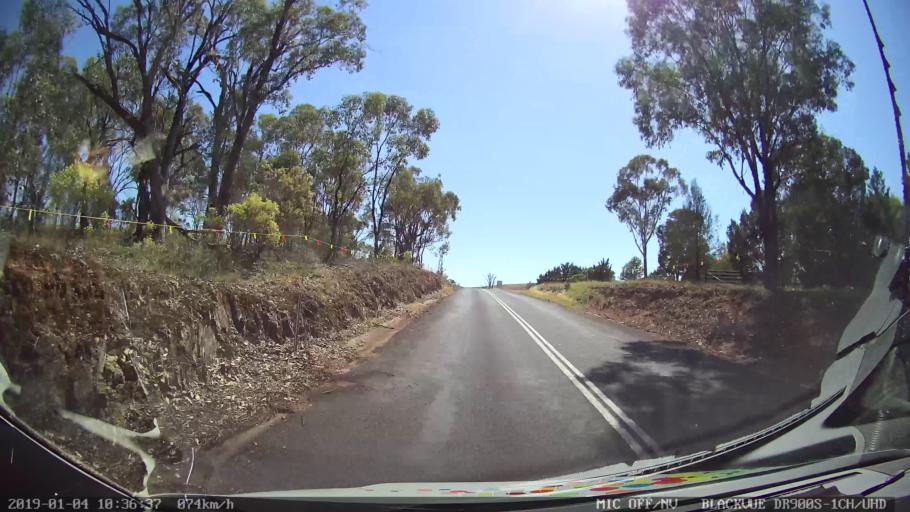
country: AU
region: New South Wales
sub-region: Cabonne
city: Canowindra
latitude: -33.3023
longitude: 148.6864
